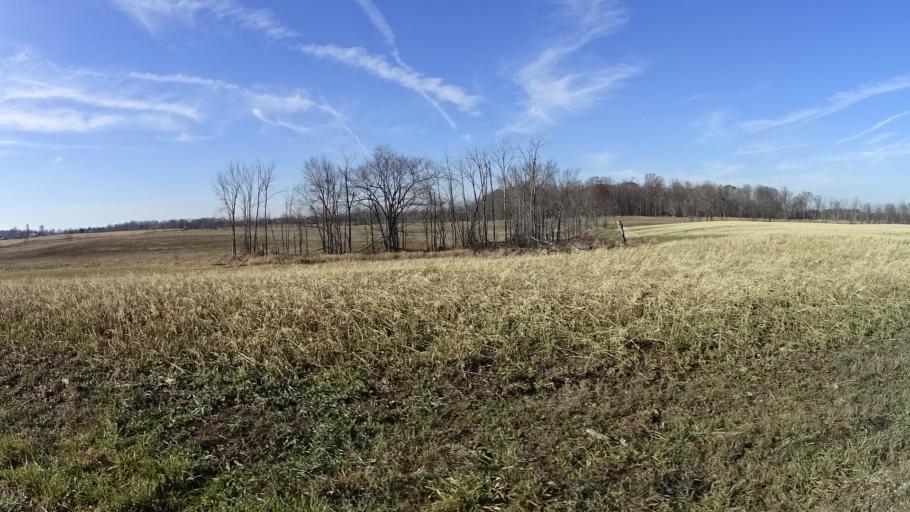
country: US
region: Ohio
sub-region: Huron County
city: New London
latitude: 41.0627
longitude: -82.2798
